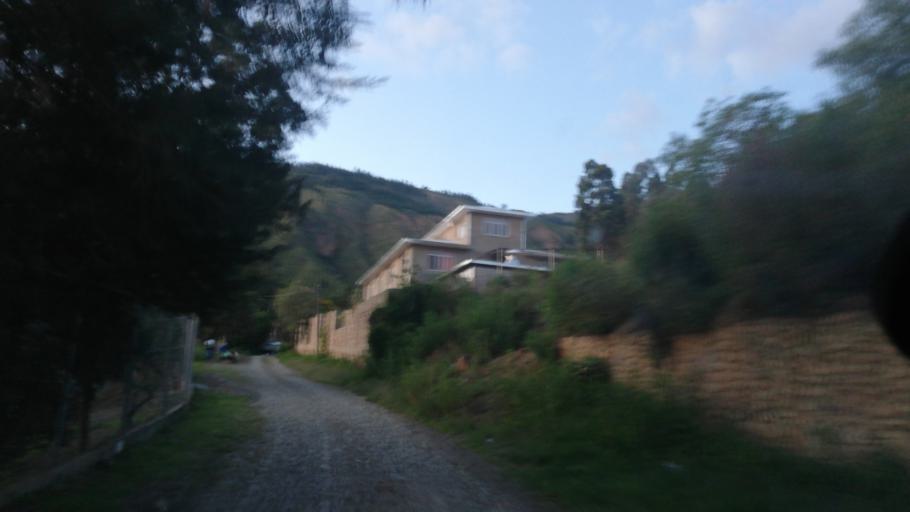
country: BO
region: Cochabamba
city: Cochabamba
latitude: -17.3199
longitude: -66.2077
